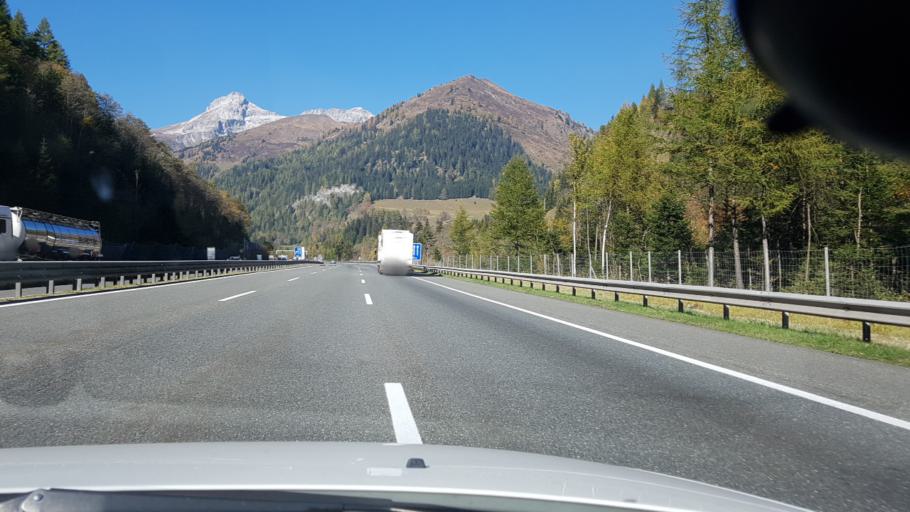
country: AT
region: Salzburg
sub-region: Politischer Bezirk Tamsweg
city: Zederhaus
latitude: 47.1757
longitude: 13.4471
